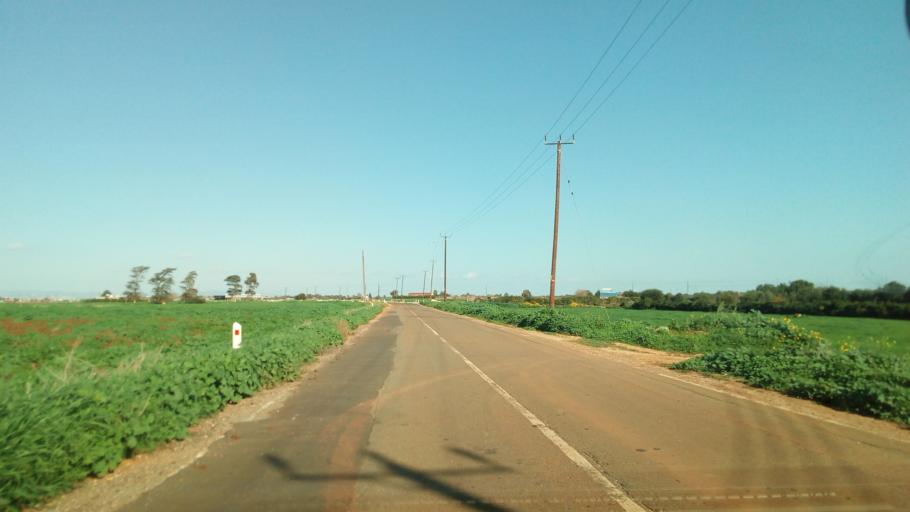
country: CY
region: Ammochostos
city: Avgorou
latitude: 35.0051
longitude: 33.8444
